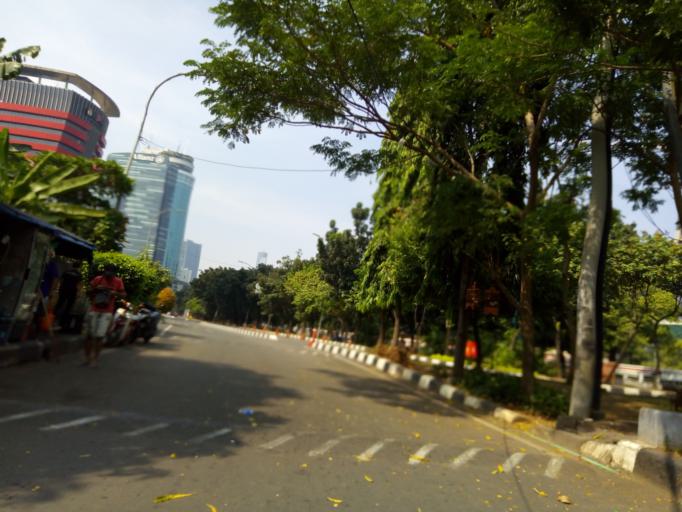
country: ID
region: Jakarta Raya
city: Jakarta
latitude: -6.2062
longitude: 106.8297
